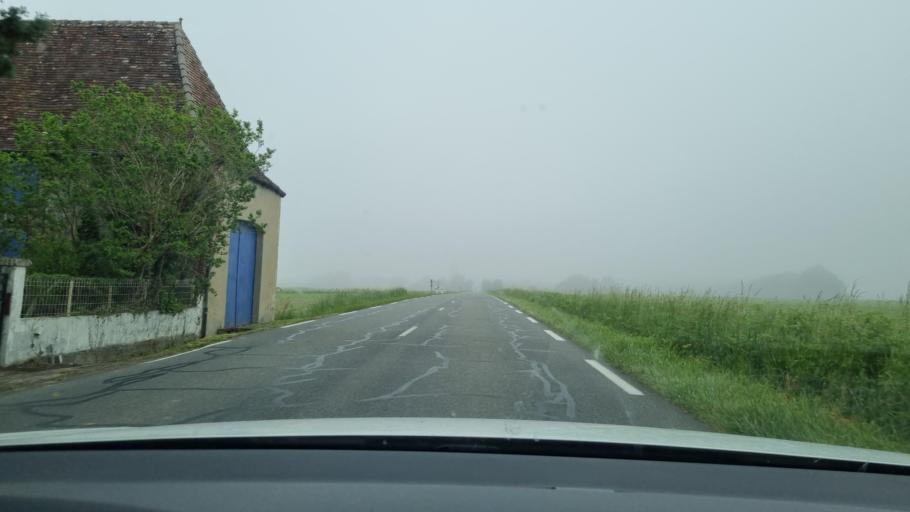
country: FR
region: Aquitaine
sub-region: Departement des Landes
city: Amou
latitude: 43.5294
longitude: -0.6998
